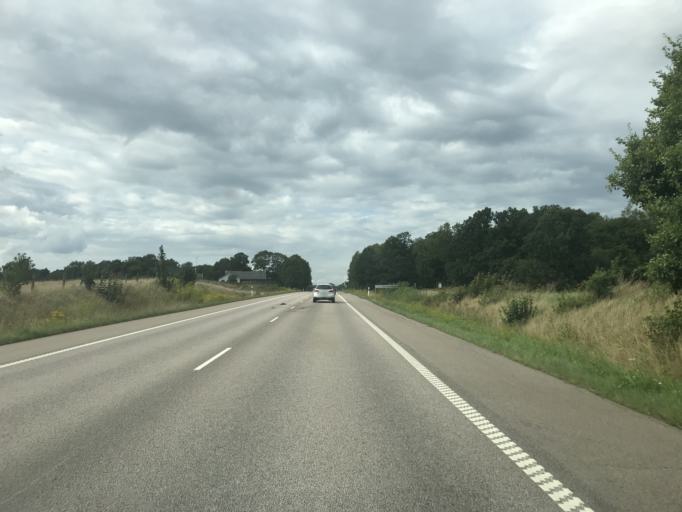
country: SE
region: Skane
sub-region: Hassleholms Kommun
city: Hassleholm
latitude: 56.1374
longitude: 13.8085
